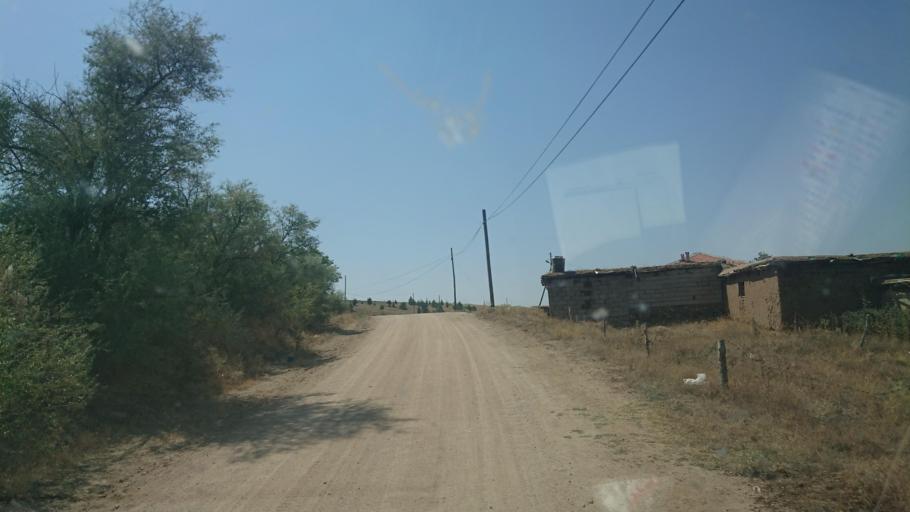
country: TR
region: Aksaray
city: Agacoren
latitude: 38.8175
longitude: 33.9543
